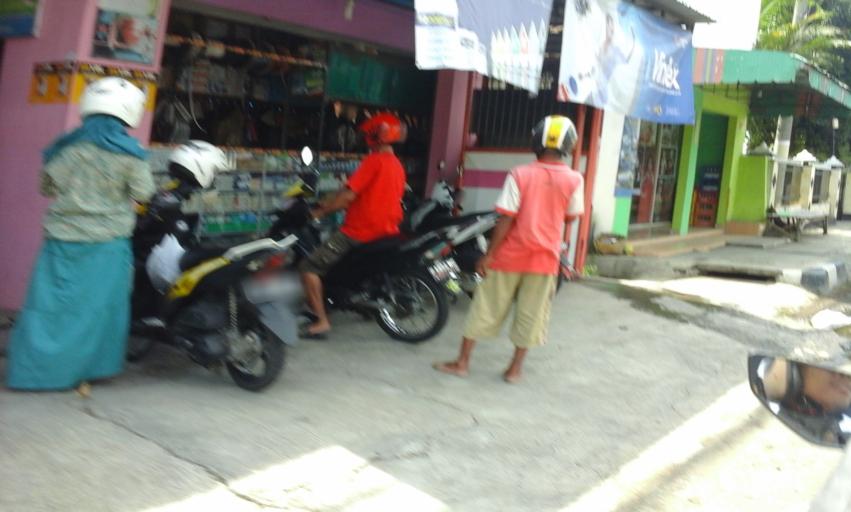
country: ID
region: East Java
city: Klatakan
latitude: -8.1808
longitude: 114.3823
